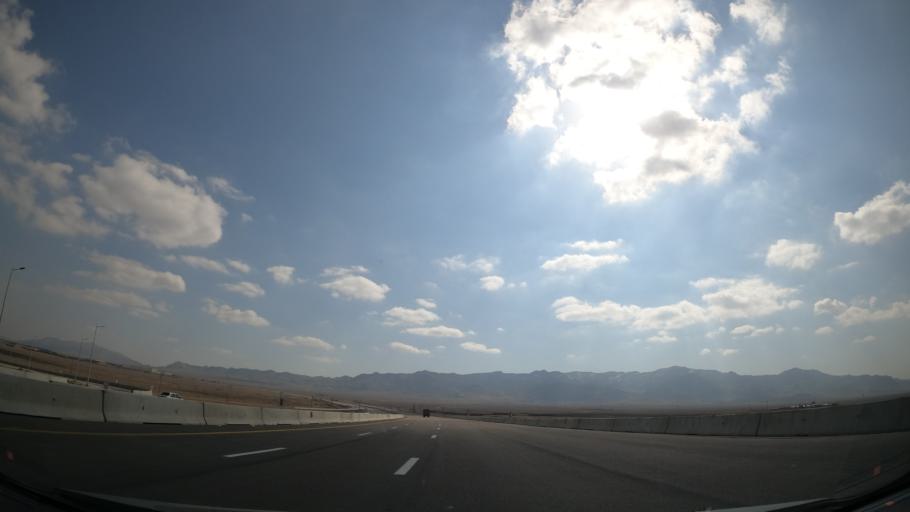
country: IR
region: Alborz
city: Eshtehard
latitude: 35.7307
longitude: 50.5610
